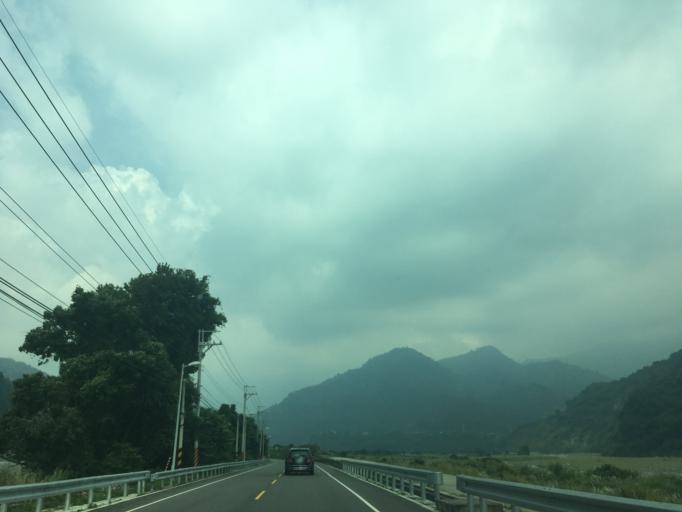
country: TW
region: Taiwan
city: Fengyuan
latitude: 24.2964
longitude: 120.8851
